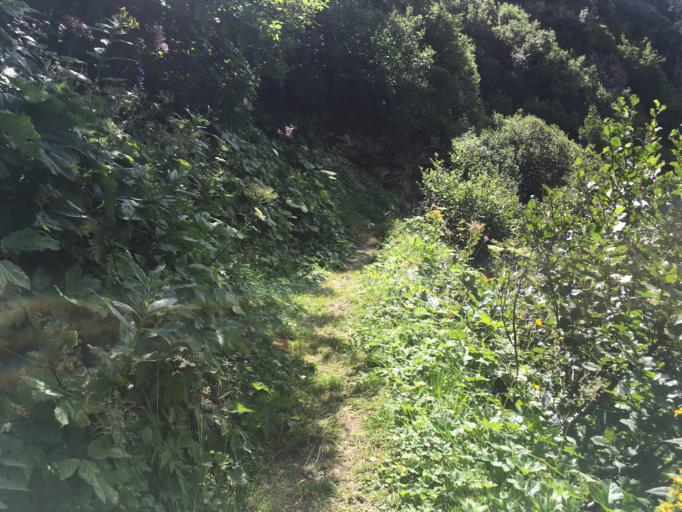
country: CH
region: Grisons
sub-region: Maloja District
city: Silvaplana
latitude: 46.4609
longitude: 9.6671
